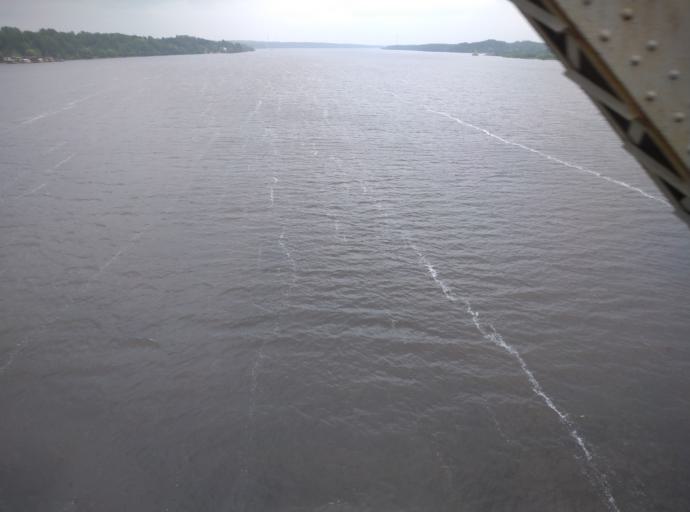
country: RU
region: Kostroma
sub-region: Kostromskoy Rayon
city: Kostroma
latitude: 57.7387
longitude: 40.9539
